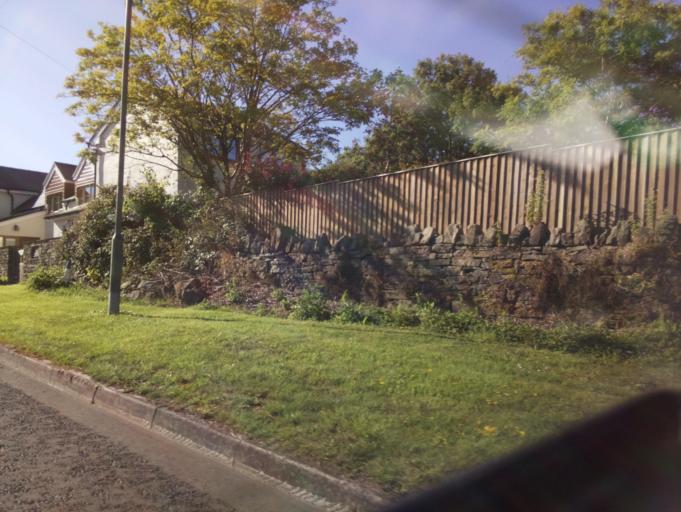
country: GB
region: England
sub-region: Gloucestershire
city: Coleford
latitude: 51.7961
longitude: -2.6024
